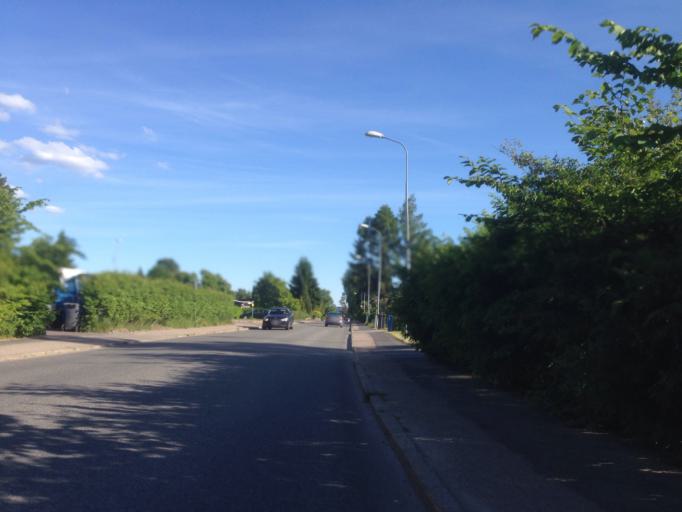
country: SE
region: Dalarna
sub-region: Ludvika Kommun
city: Ludvika
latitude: 60.1236
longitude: 15.1917
